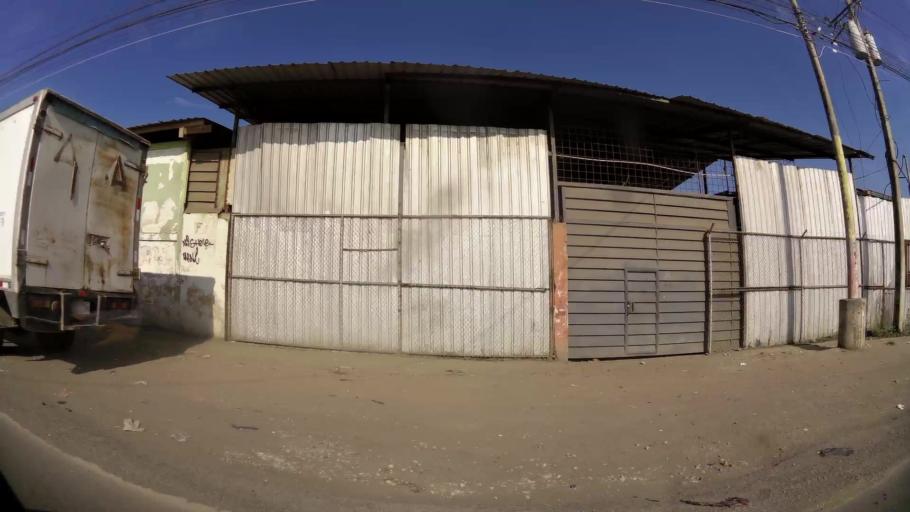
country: EC
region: Guayas
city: Eloy Alfaro
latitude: -2.1750
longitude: -79.8328
